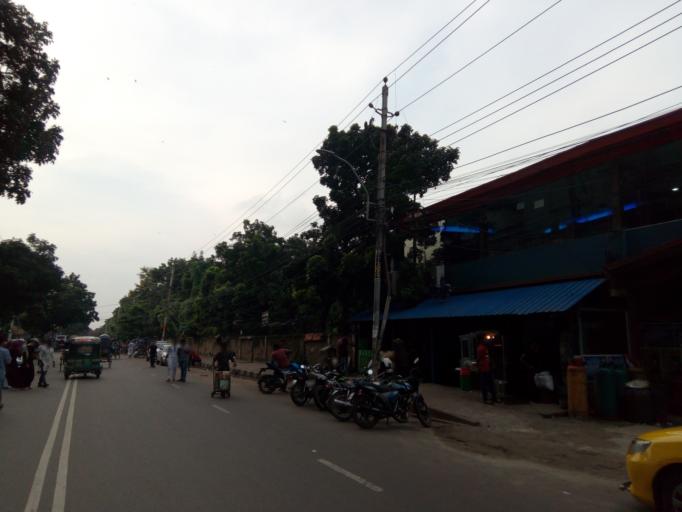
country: BD
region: Dhaka
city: Azimpur
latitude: 23.7218
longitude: 90.3879
